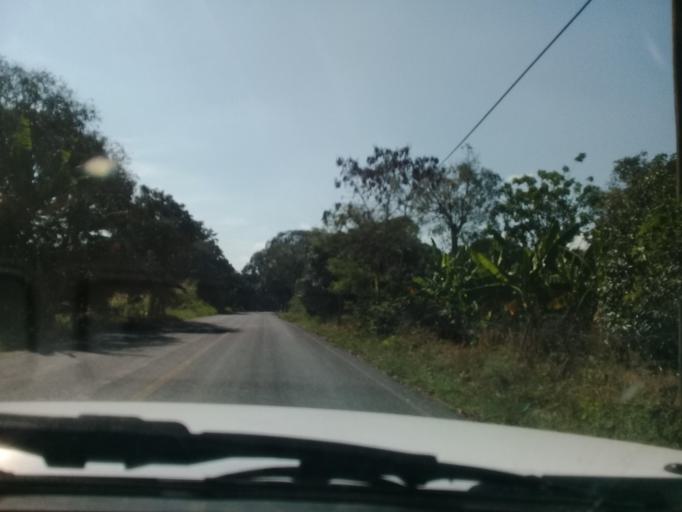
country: MX
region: Veracruz
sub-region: Emiliano Zapata
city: Plan del Rio
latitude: 19.4211
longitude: -96.6155
